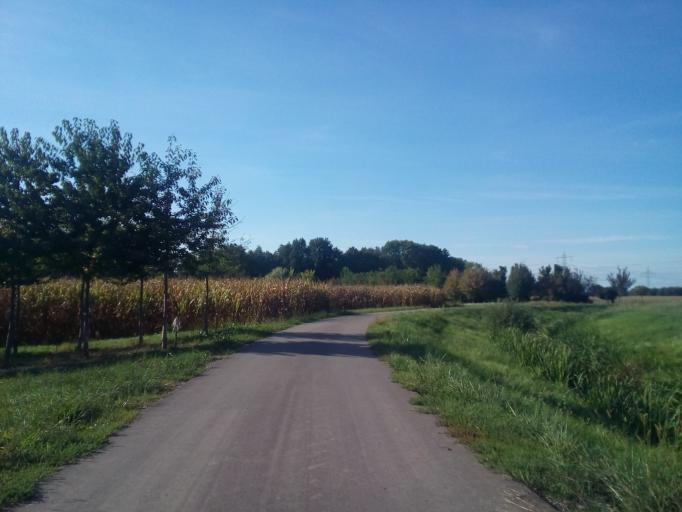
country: DE
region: Baden-Wuerttemberg
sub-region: Karlsruhe Region
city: Zell
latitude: 48.6689
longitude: 8.0717
